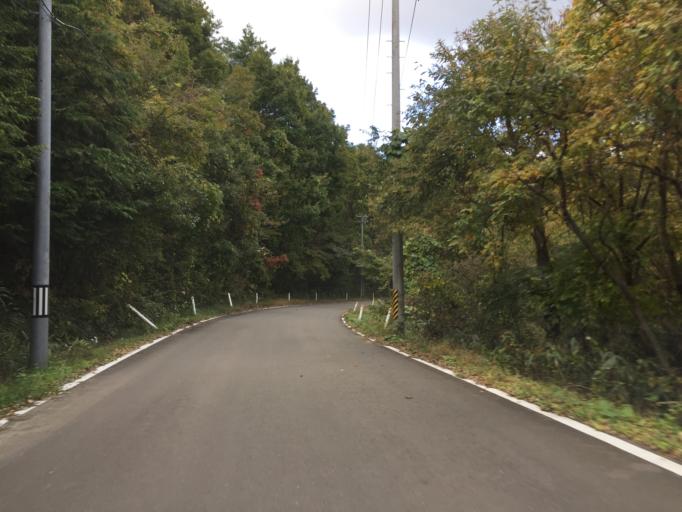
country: JP
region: Miyagi
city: Marumori
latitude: 37.8127
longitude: 140.7854
